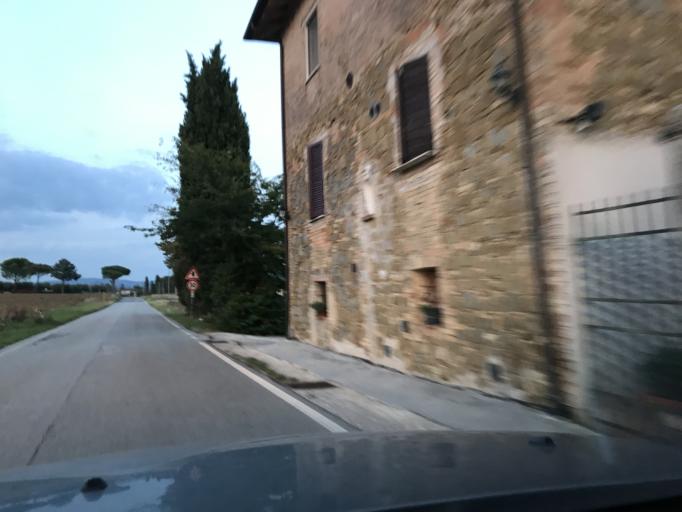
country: IT
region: Umbria
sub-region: Provincia di Perugia
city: Via Lippia
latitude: 43.0912
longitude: 12.4879
